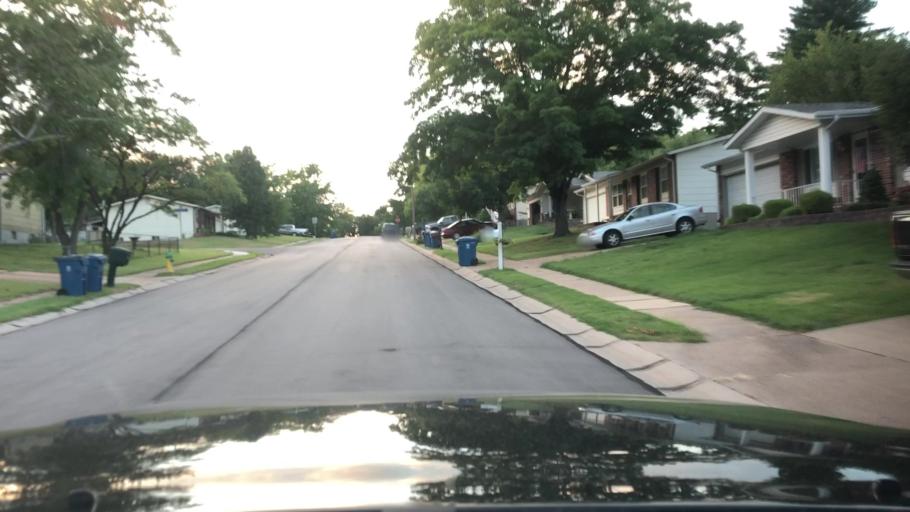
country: US
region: Missouri
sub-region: Saint Charles County
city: Saint Charles
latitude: 38.8116
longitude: -90.5064
